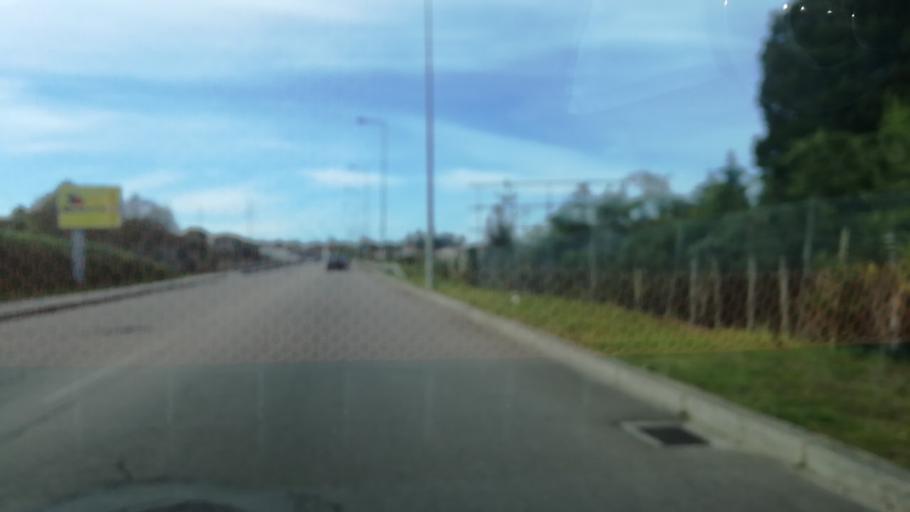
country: PT
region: Porto
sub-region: Valongo
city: Ermesinde
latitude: 41.2242
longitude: -8.5646
